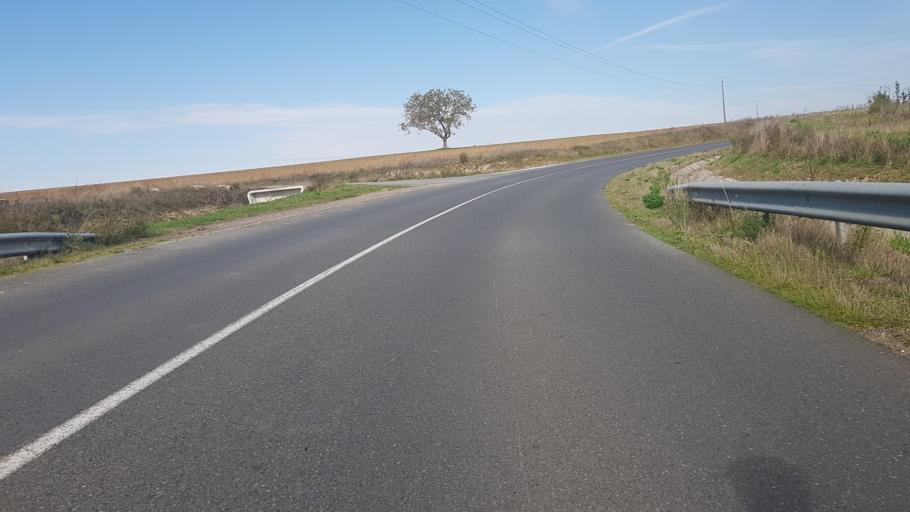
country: FR
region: Poitou-Charentes
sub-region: Departement de la Vienne
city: Chasseneuil-du-Poitou
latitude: 46.6434
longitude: 0.3491
